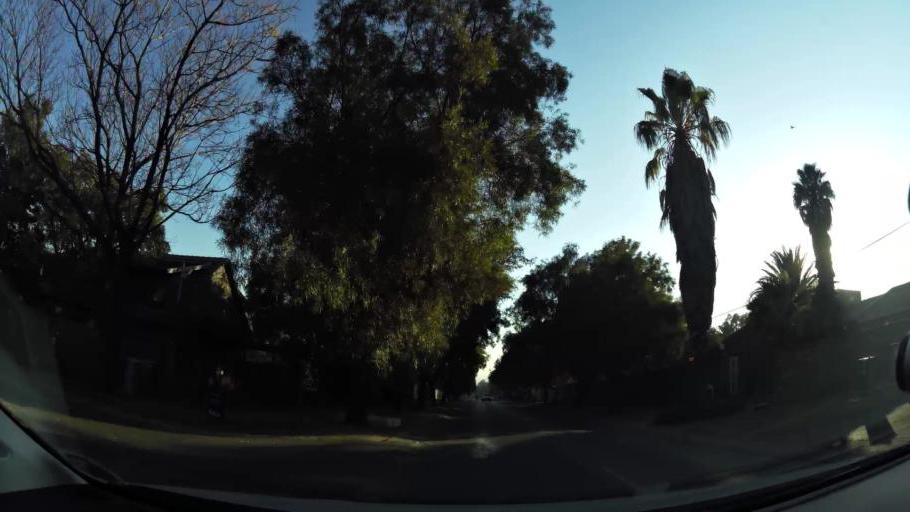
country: ZA
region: Gauteng
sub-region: City of Johannesburg Metropolitan Municipality
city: Midrand
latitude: -26.0530
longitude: 28.1086
